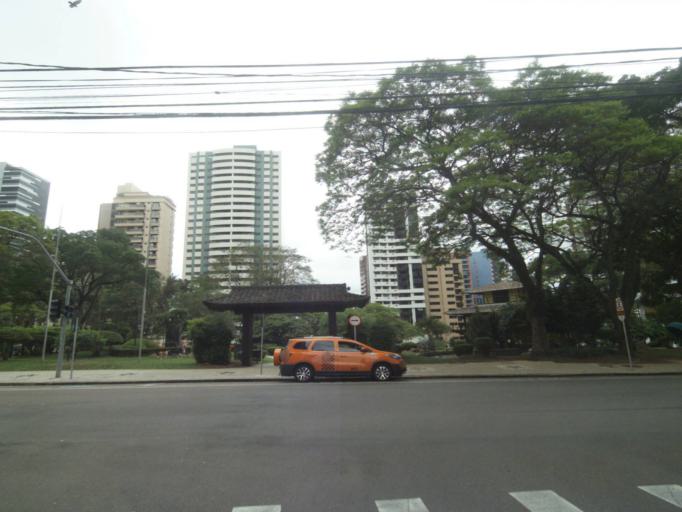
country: BR
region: Parana
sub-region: Curitiba
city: Curitiba
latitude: -25.4454
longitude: -49.2875
